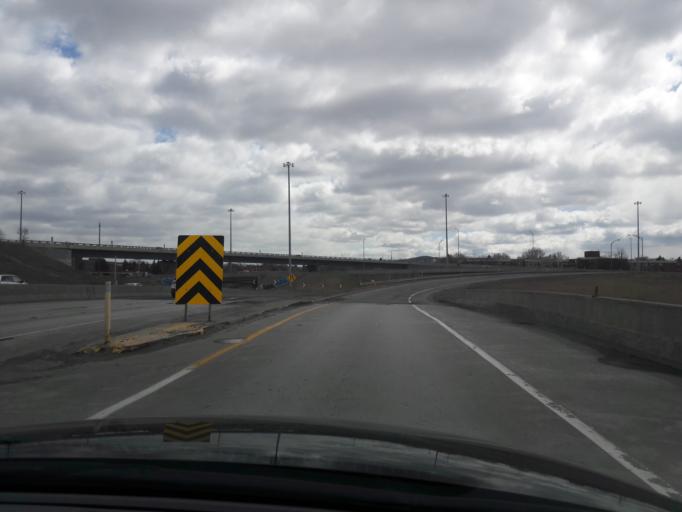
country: CA
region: Quebec
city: Mont-Royal
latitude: 45.5272
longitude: -73.6541
